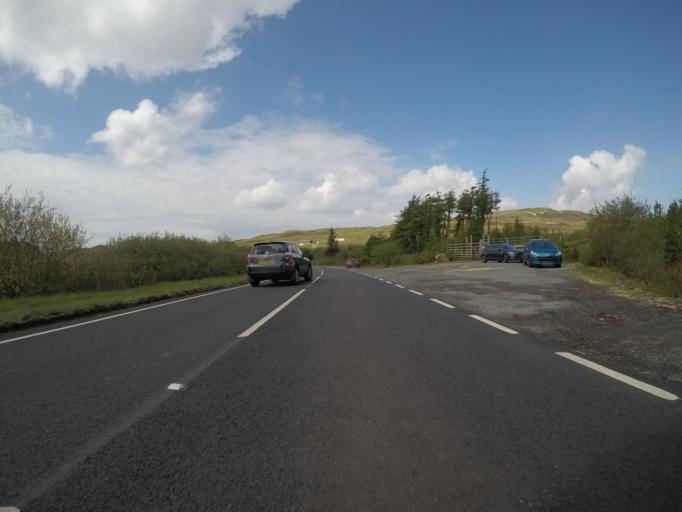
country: GB
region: Scotland
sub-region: Highland
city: Portree
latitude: 57.5298
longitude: -6.3491
